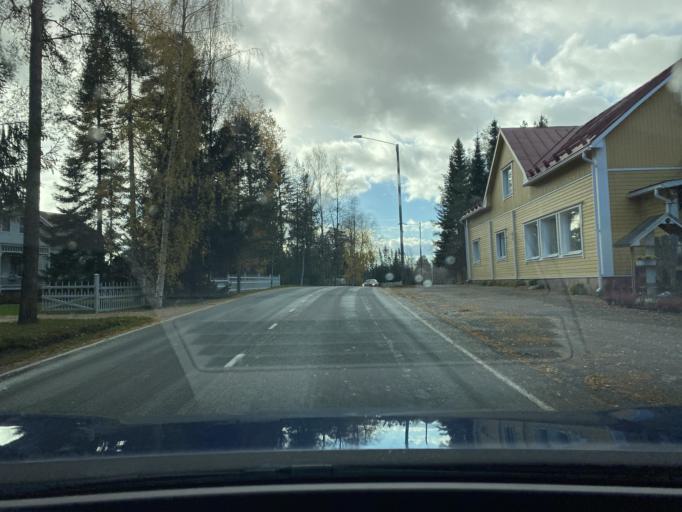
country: FI
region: Varsinais-Suomi
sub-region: Loimaa
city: Aura
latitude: 60.7160
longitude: 22.6000
